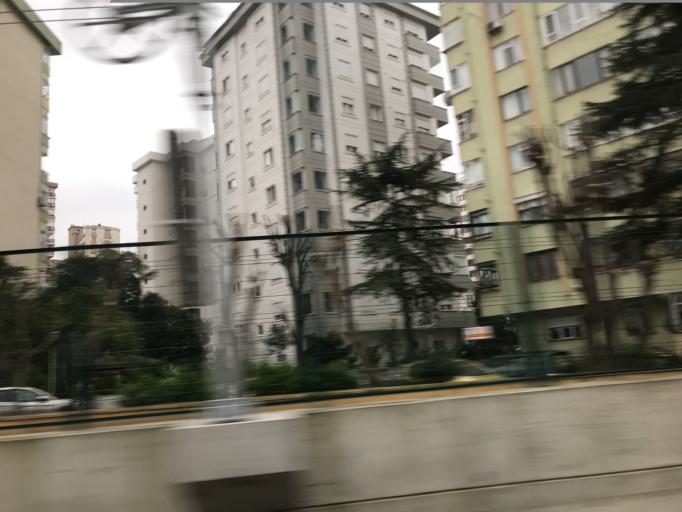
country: TR
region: Istanbul
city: UEskuedar
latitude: 40.9785
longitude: 29.0593
